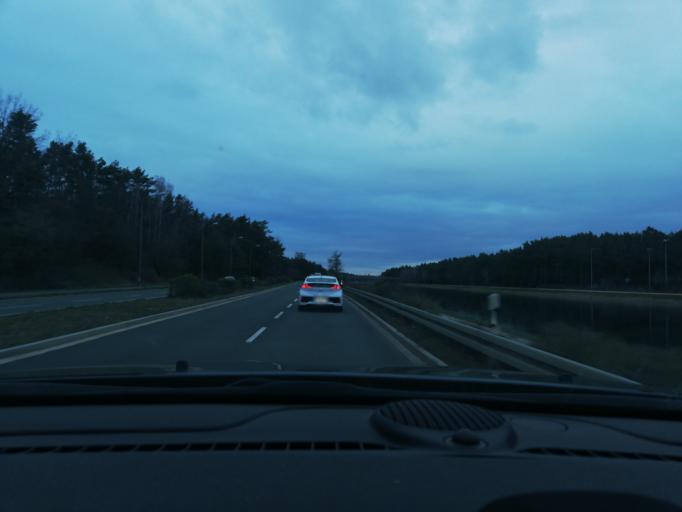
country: DE
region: Bavaria
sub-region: Regierungsbezirk Mittelfranken
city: Erlangen
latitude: 49.6028
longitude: 10.9717
